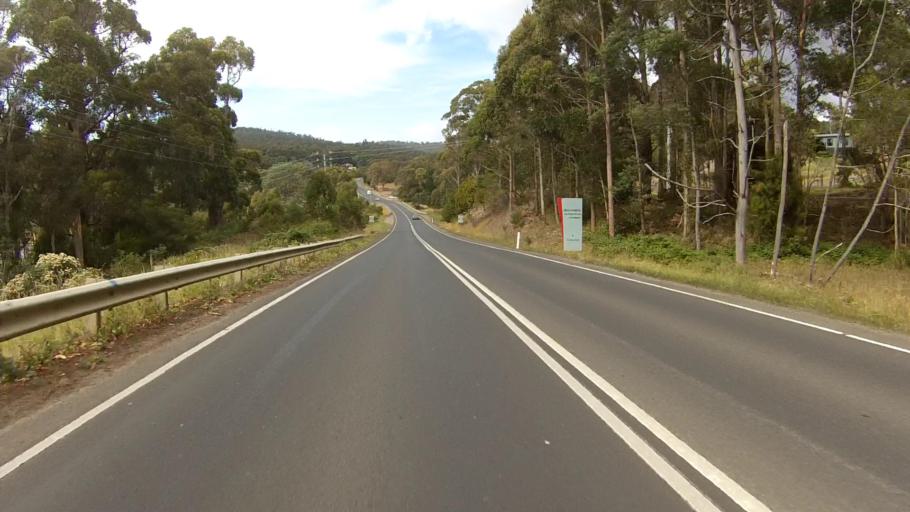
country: AU
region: Tasmania
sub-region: Kingborough
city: Margate
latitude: -43.0705
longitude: 147.2567
